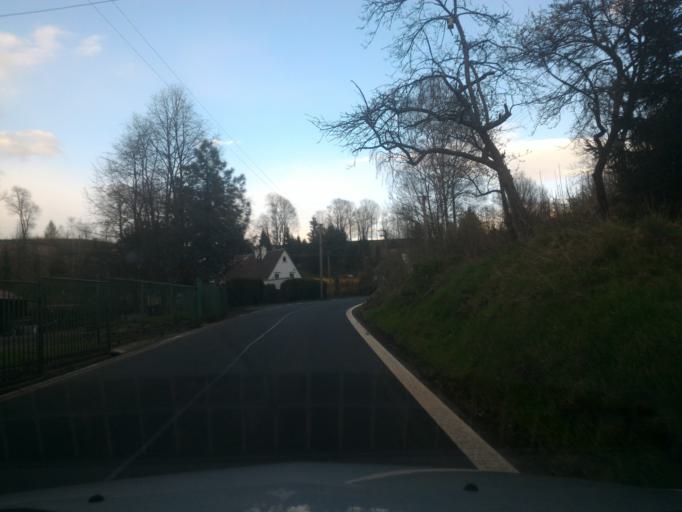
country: CZ
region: Ustecky
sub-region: Okres Decin
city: Krasna Lipa
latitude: 50.9158
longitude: 14.5240
